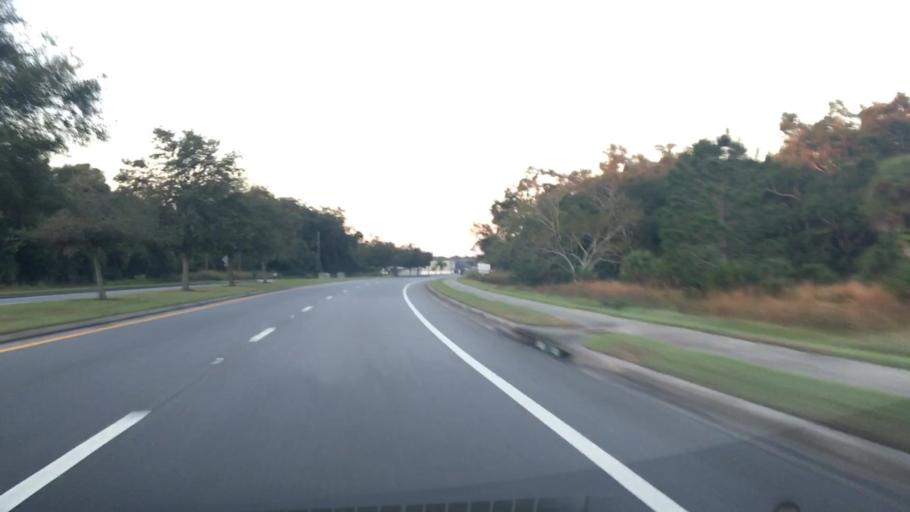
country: US
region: Florida
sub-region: Seminole County
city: Midway
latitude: 28.7574
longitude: -81.2319
